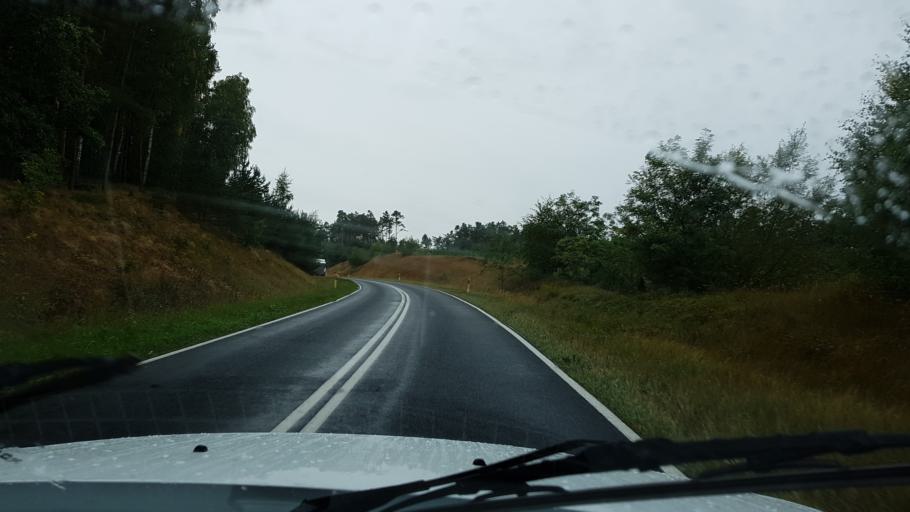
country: PL
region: West Pomeranian Voivodeship
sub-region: Powiat gryfinski
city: Widuchowa
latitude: 53.0721
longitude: 14.3673
